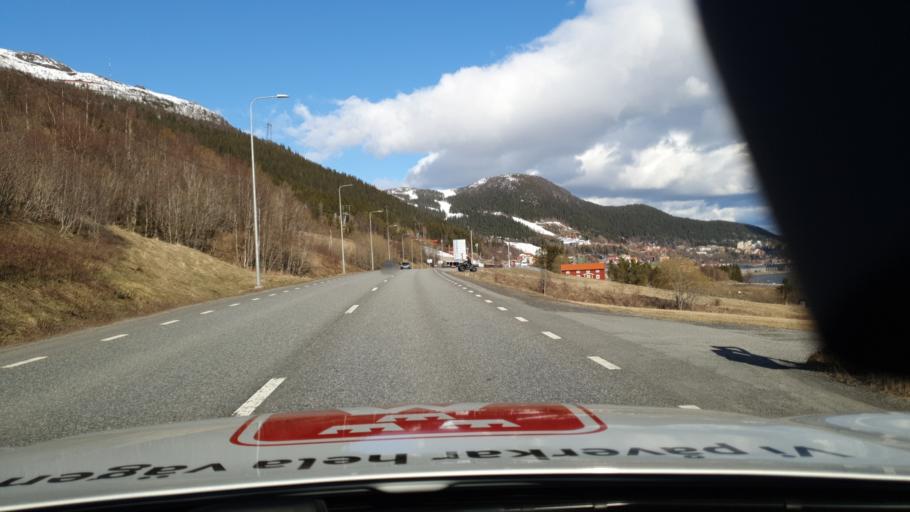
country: SE
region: Jaemtland
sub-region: Are Kommun
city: Are
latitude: 63.4060
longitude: 13.0457
